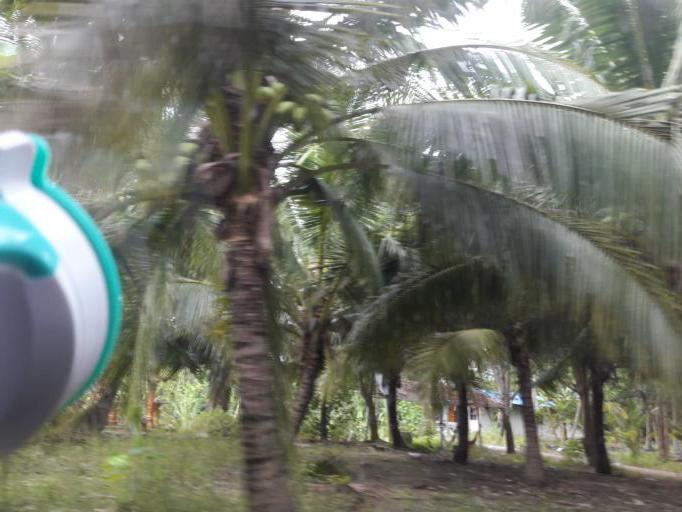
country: TH
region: Ratchaburi
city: Damnoen Saduak
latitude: 13.5233
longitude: 100.0075
